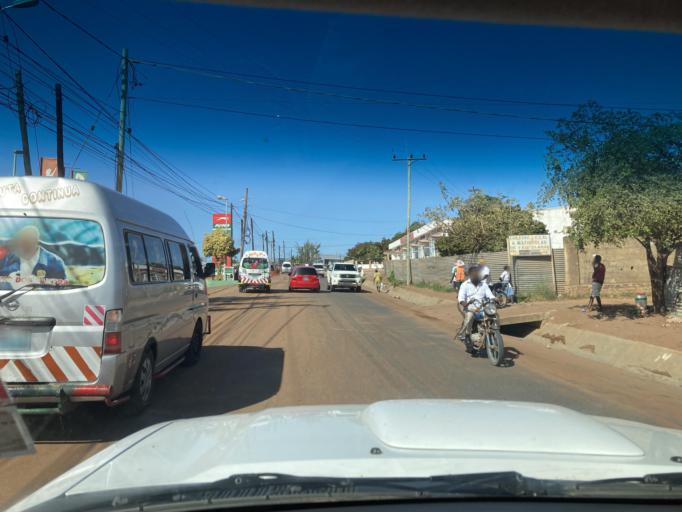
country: MZ
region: Cabo Delgado
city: Pemba
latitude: -12.9823
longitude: 40.5413
